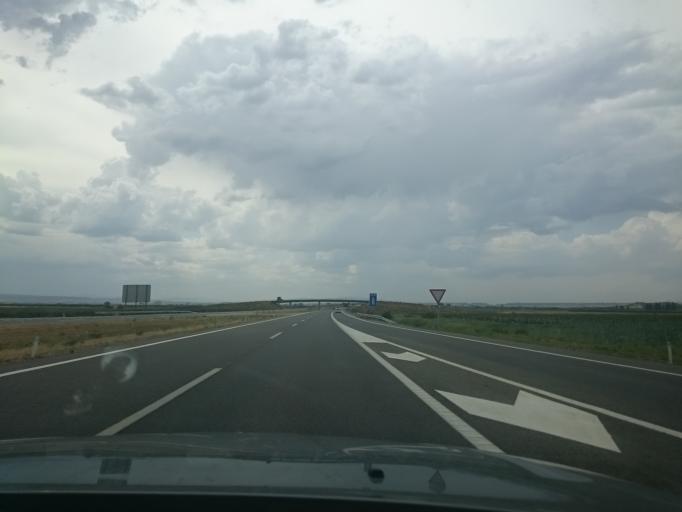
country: ES
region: Navarre
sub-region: Provincia de Navarra
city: Fontellas
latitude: 42.0148
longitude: -1.6055
